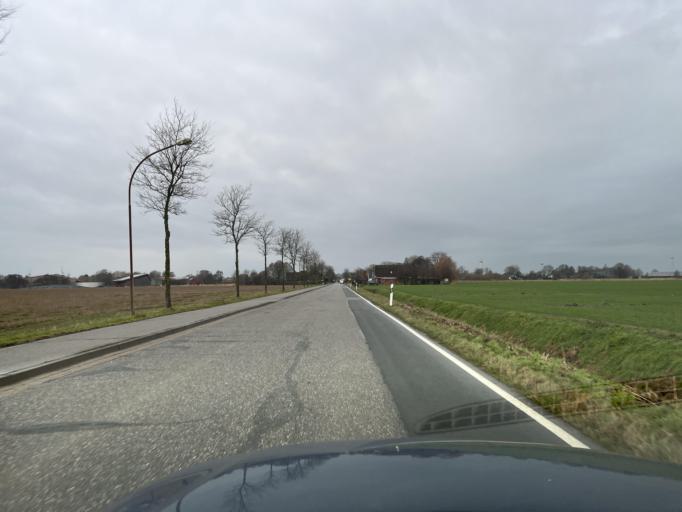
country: DE
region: Schleswig-Holstein
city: Norddeich
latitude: 54.2145
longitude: 8.9096
